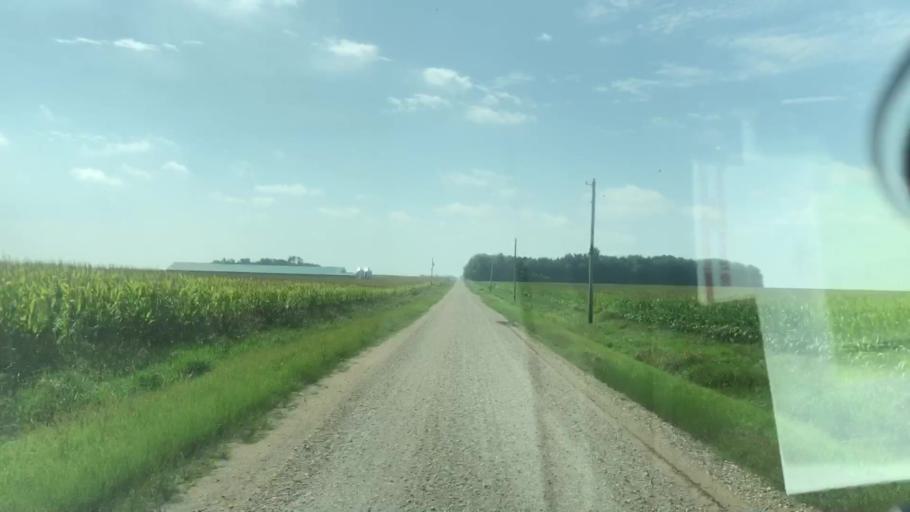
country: US
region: Iowa
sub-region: O'Brien County
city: Sheldon
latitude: 43.1968
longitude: -95.9414
